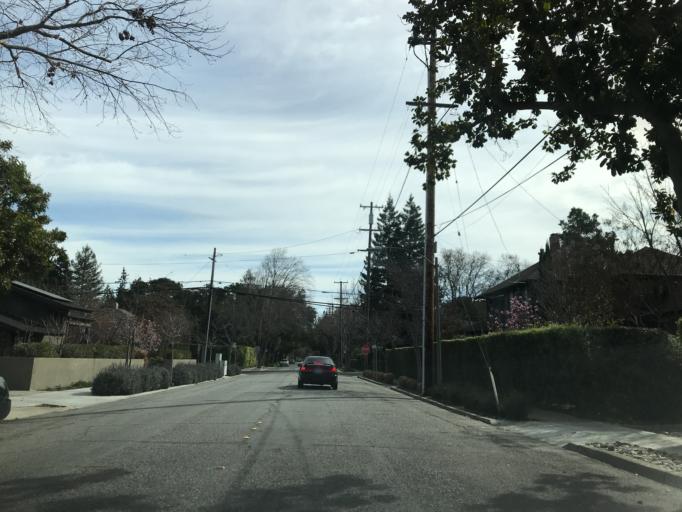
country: US
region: California
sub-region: Santa Clara County
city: Palo Alto
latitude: 37.4428
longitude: -122.1536
